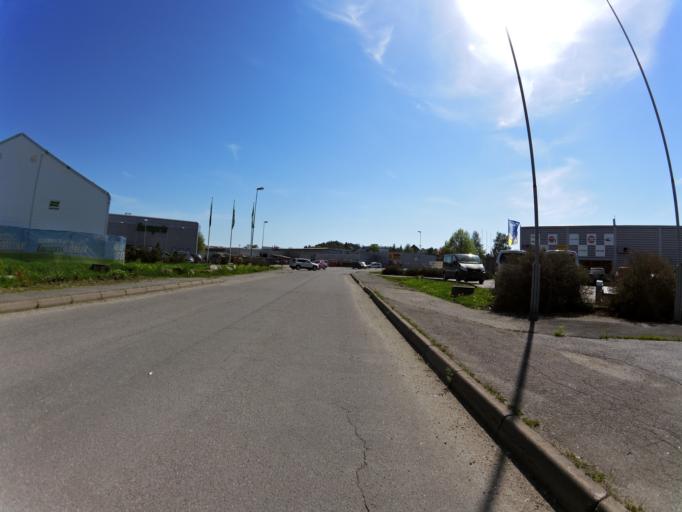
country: NO
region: Ostfold
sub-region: Fredrikstad
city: Fredrikstad
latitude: 59.2348
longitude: 10.9070
